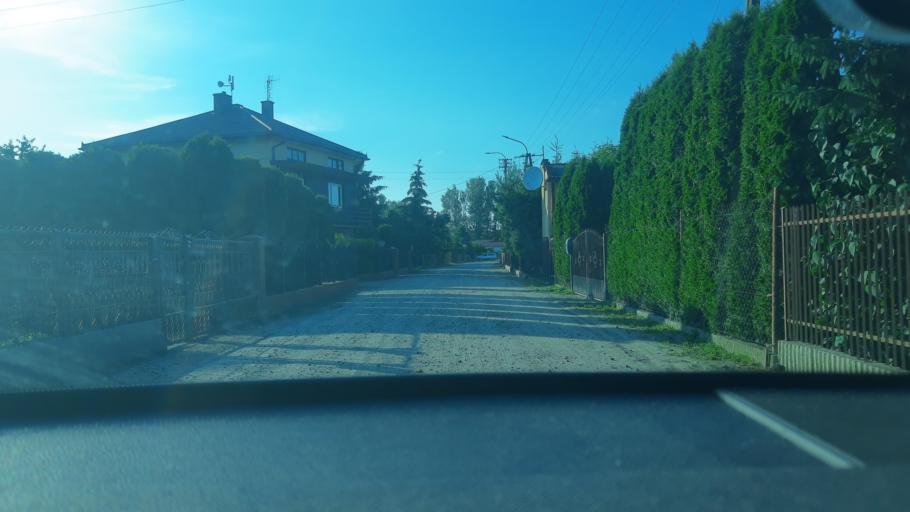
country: PL
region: Lodz Voivodeship
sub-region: Powiat sieradzki
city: Burzenin
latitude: 51.4563
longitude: 18.8420
